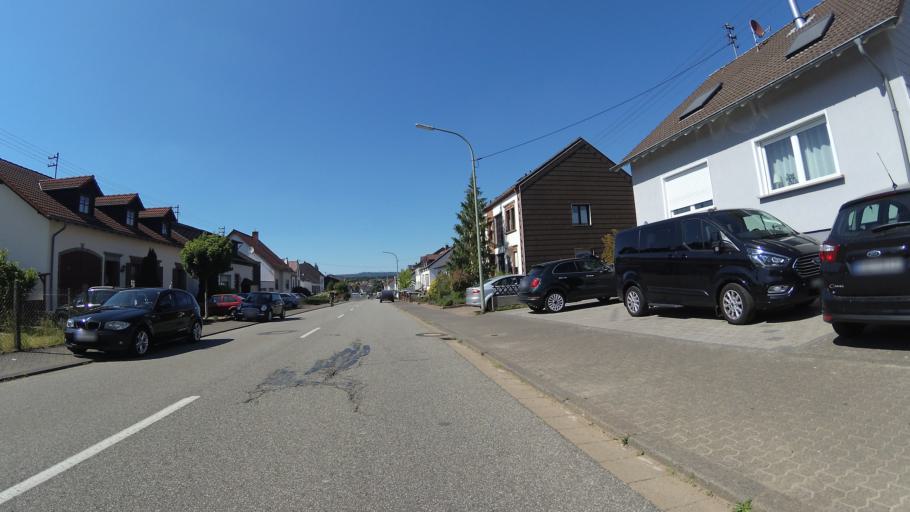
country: DE
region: Saarland
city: Saarwellingen
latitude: 49.3472
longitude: 6.8105
